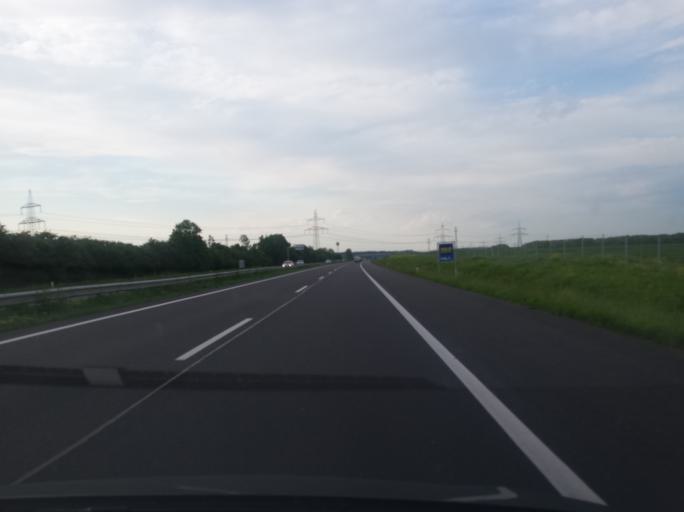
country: AT
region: Burgenland
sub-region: Eisenstadt-Umgebung
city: Hornstein
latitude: 47.8696
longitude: 16.4181
